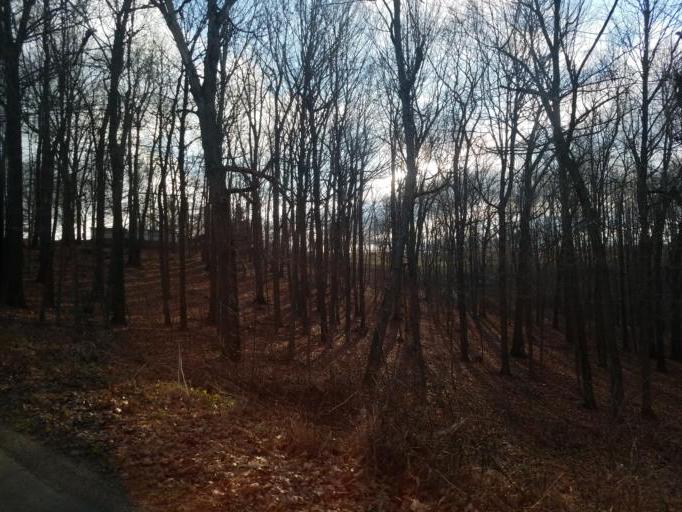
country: US
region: Ohio
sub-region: Ashland County
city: Loudonville
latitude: 40.6212
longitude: -82.3712
